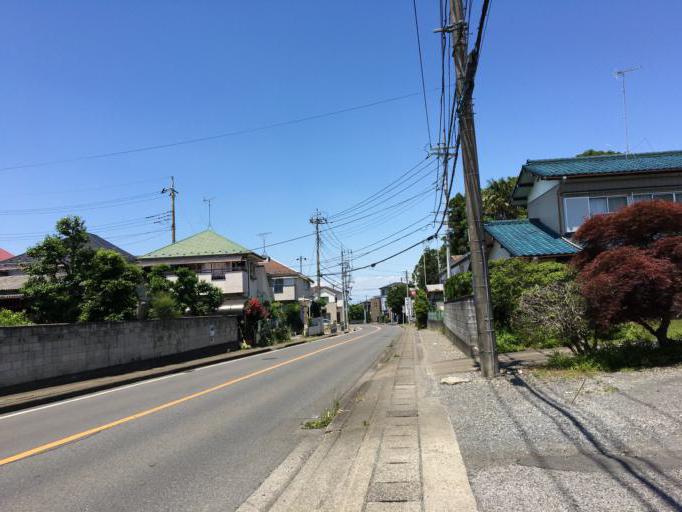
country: JP
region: Saitama
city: Sakado
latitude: 35.9402
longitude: 139.3888
